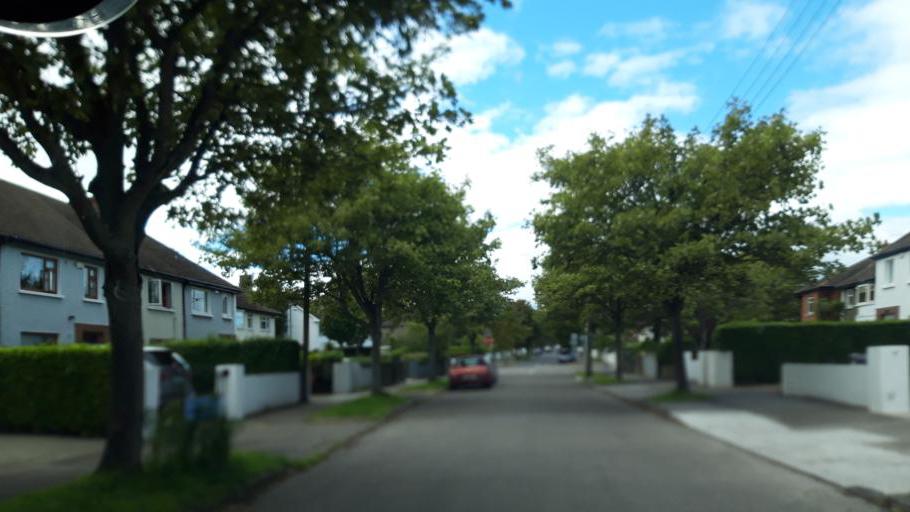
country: IE
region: Leinster
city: Dollymount
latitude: 53.3612
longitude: -6.1876
